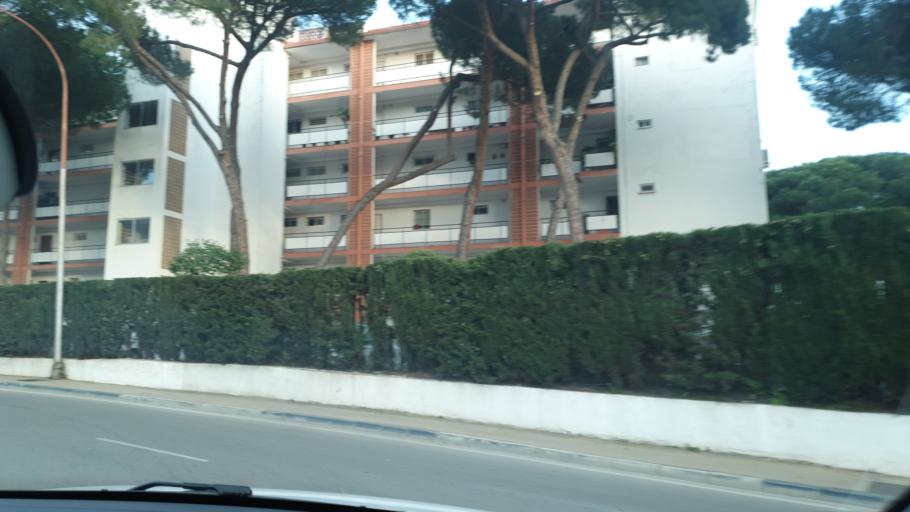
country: ES
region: Andalusia
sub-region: Provincia de Malaga
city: Marbella
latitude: 36.5147
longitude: -4.8965
